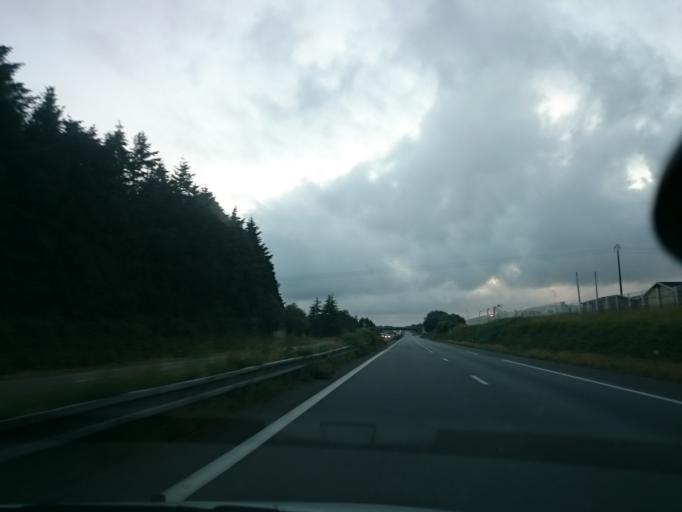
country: FR
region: Brittany
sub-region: Departement du Finistere
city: Quimperle
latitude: 47.8656
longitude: -3.5807
